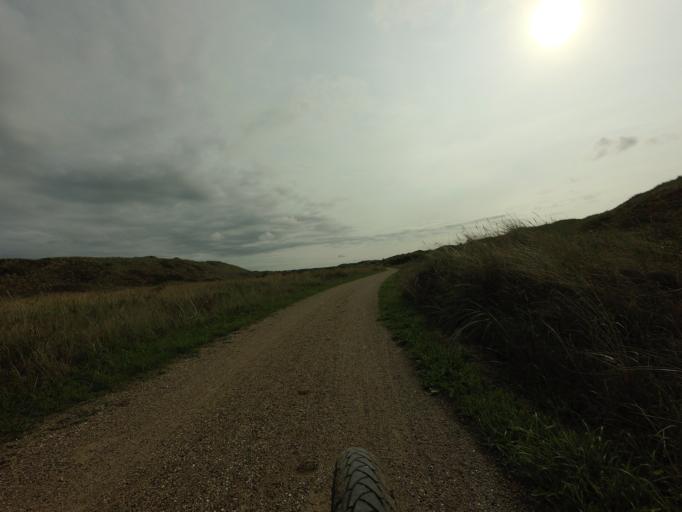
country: DK
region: North Denmark
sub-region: Hjorring Kommune
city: Sindal
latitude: 57.5884
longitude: 10.1341
